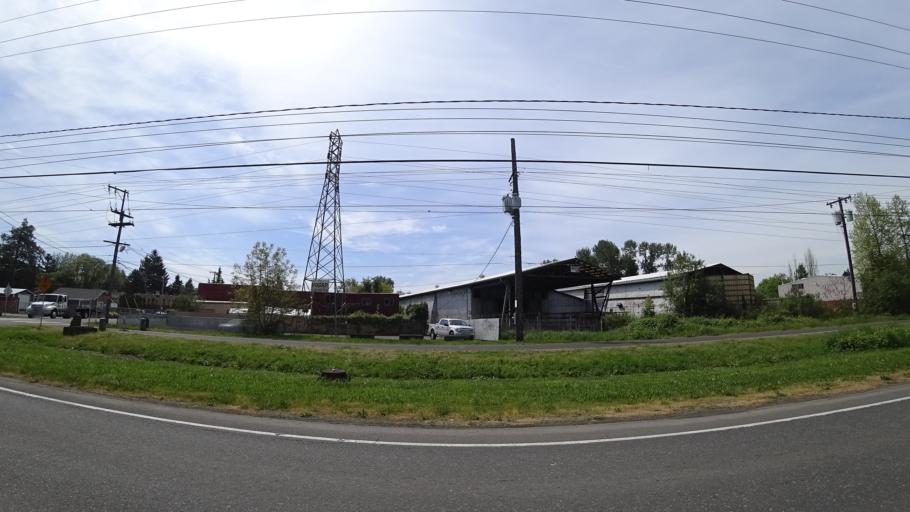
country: US
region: Oregon
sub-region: Clackamas County
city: Milwaukie
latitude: 45.4580
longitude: -122.6049
